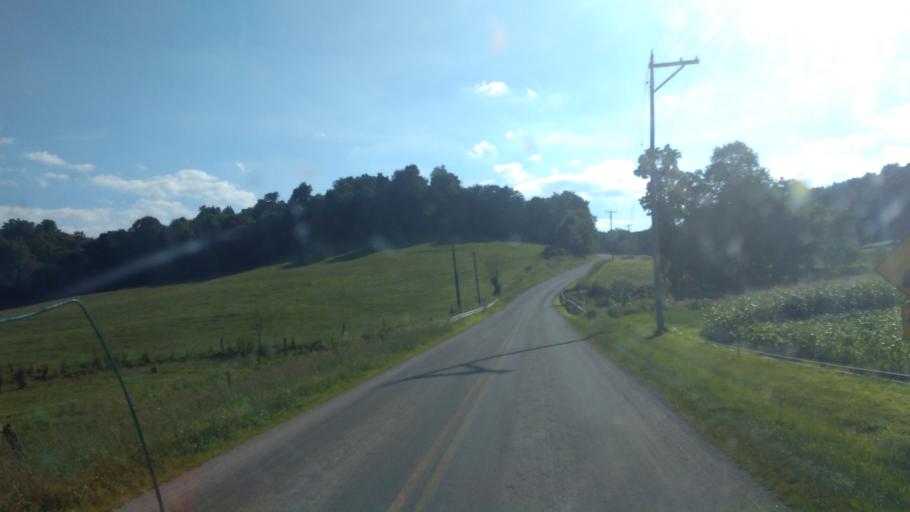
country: US
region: Ohio
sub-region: Ashland County
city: Loudonville
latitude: 40.6845
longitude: -82.2157
